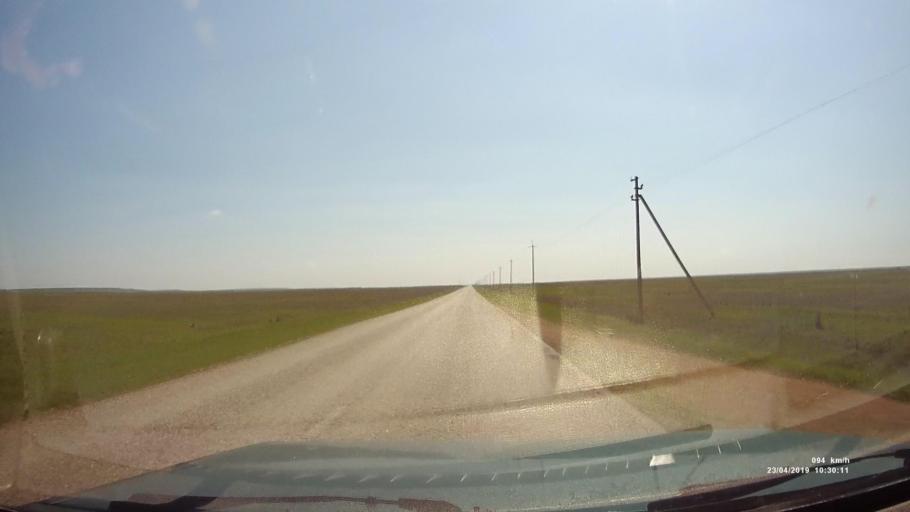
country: RU
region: Kalmykiya
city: Yashalta
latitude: 46.5938
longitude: 42.5397
